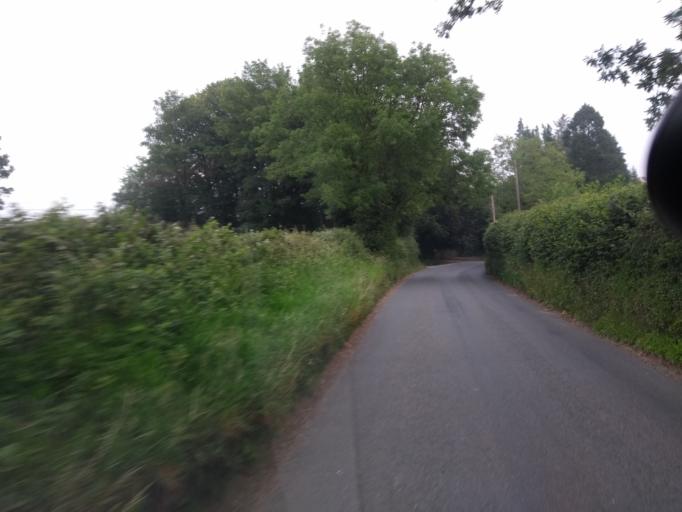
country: GB
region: England
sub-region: Somerset
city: Crewkerne
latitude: 50.8380
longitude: -2.8188
